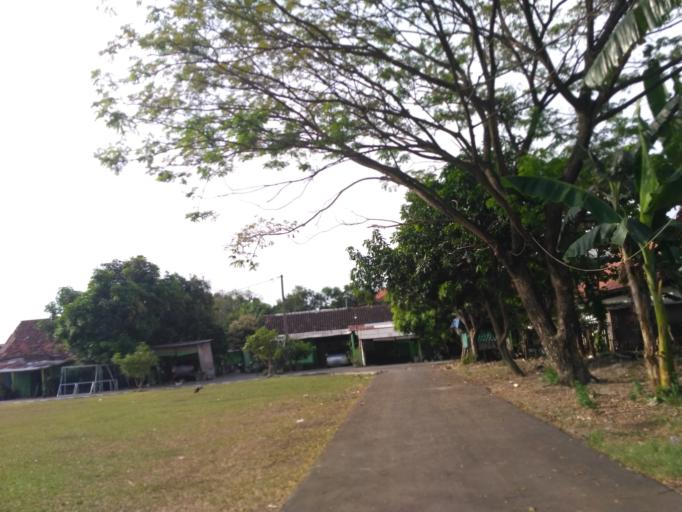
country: ID
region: Central Java
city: Semarang
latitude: -7.0122
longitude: 110.4431
